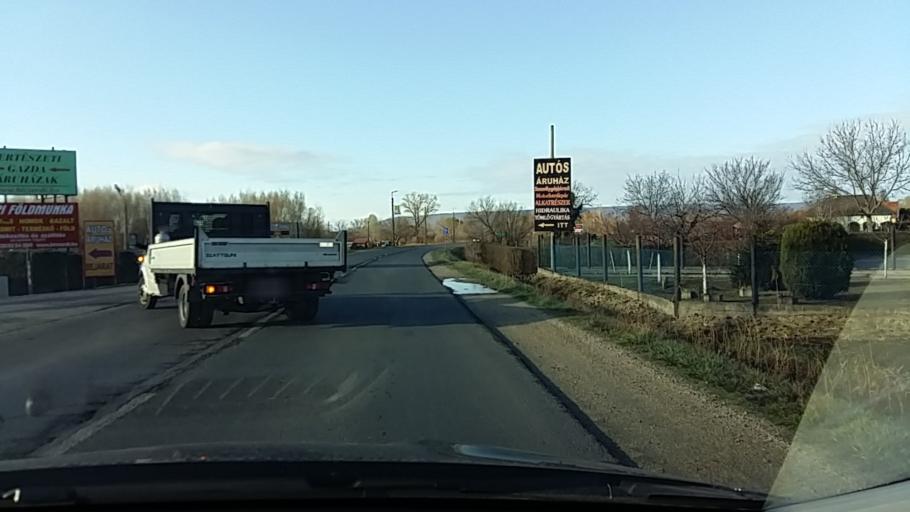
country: HU
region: Veszprem
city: Tapolca
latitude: 46.8788
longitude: 17.4479
